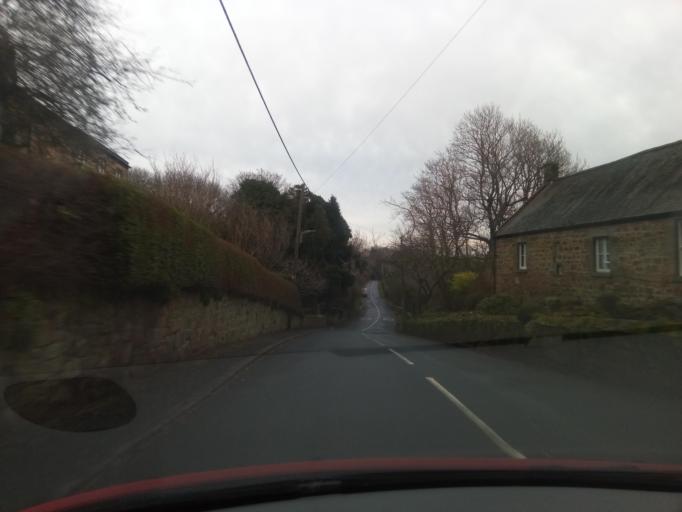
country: GB
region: England
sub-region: Northumberland
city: Whittingham
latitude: 55.4691
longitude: -1.8308
